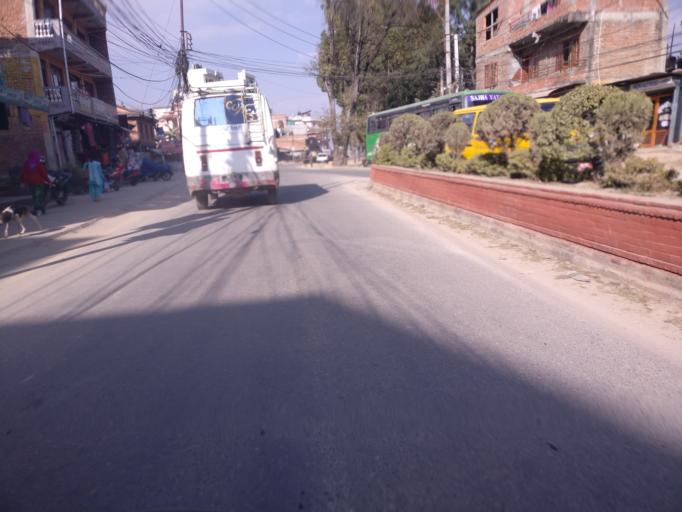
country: NP
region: Central Region
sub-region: Bagmati Zone
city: Patan
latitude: 27.6528
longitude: 85.3049
